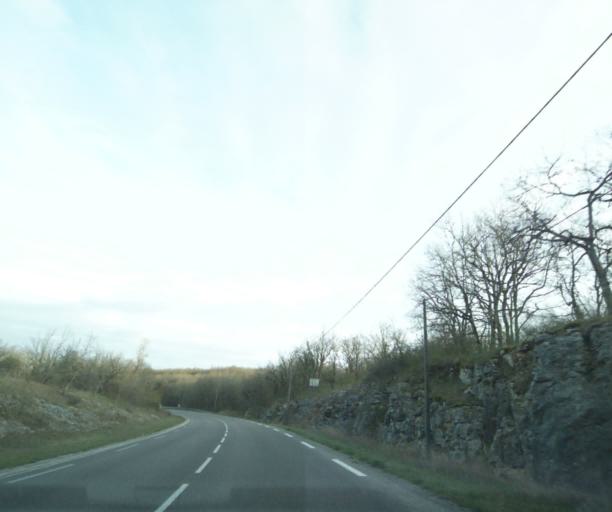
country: FR
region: Midi-Pyrenees
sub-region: Departement du Lot
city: Souillac
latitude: 44.9130
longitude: 1.4841
